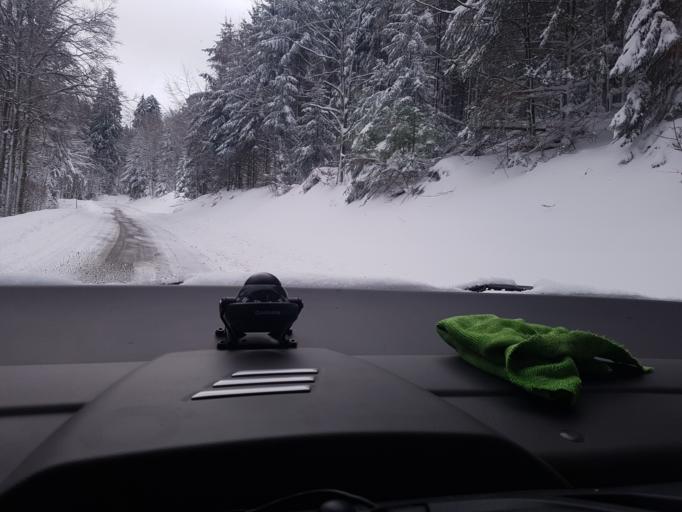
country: FR
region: Alsace
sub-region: Departement du Bas-Rhin
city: Ville
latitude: 48.3907
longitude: 7.2486
